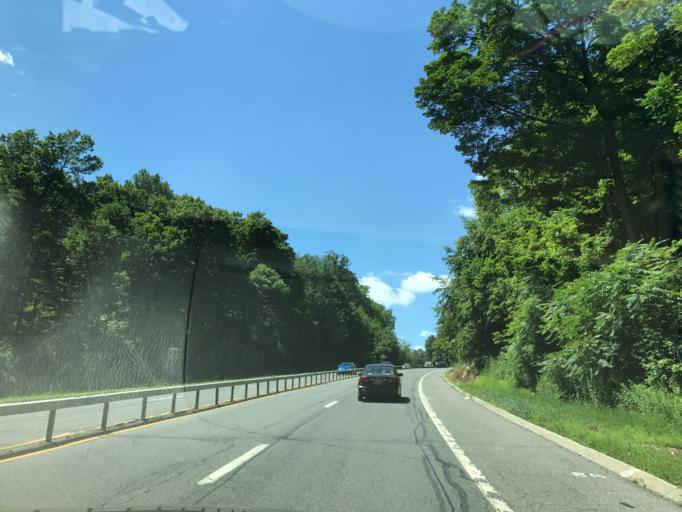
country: US
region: New York
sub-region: Dutchess County
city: Brinckerhoff
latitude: 41.4719
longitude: -73.8191
